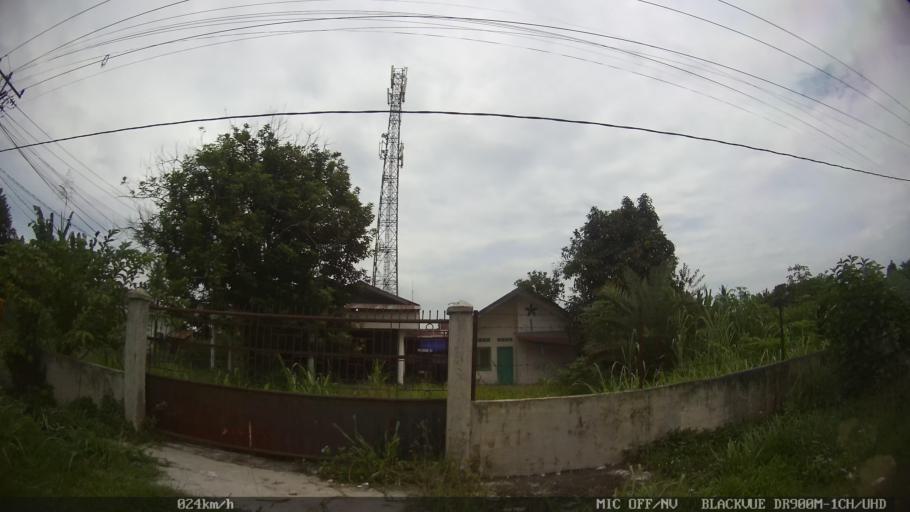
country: ID
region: North Sumatra
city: Sunggal
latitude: 3.6319
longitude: 98.5646
